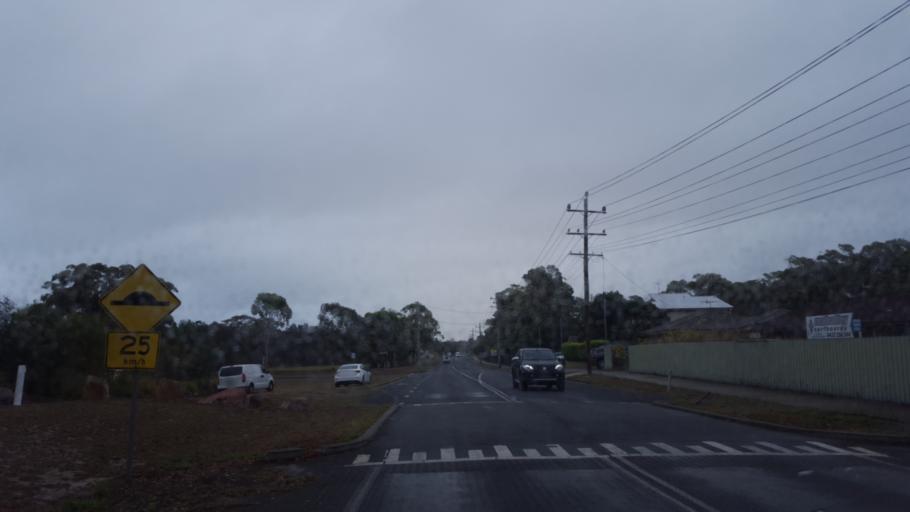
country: AU
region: New South Wales
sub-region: Port Stephens Shire
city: Anna Bay
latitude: -32.7763
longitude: 152.0934
